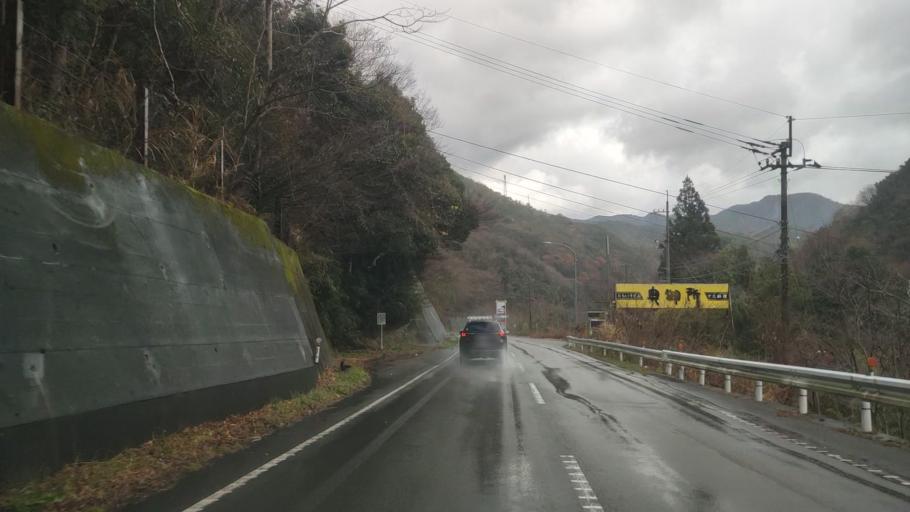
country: JP
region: Tokushima
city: Kamojimacho-jogejima
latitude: 34.1650
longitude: 134.3381
